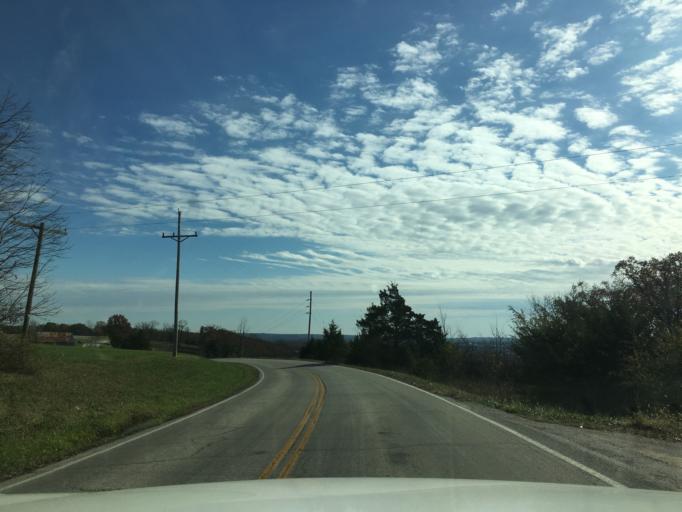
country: US
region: Missouri
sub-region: Osage County
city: Linn
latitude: 38.4204
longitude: -91.8251
